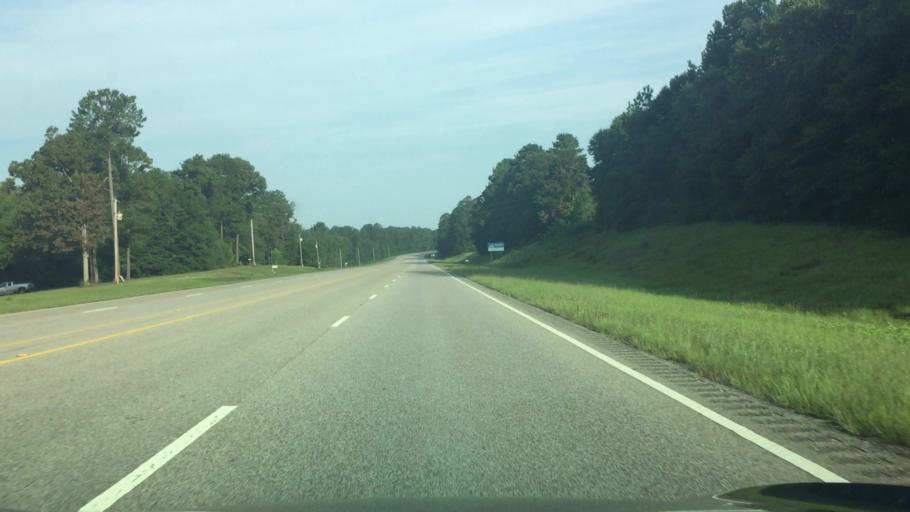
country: US
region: Alabama
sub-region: Covington County
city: Andalusia
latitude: 31.4037
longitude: -86.5931
